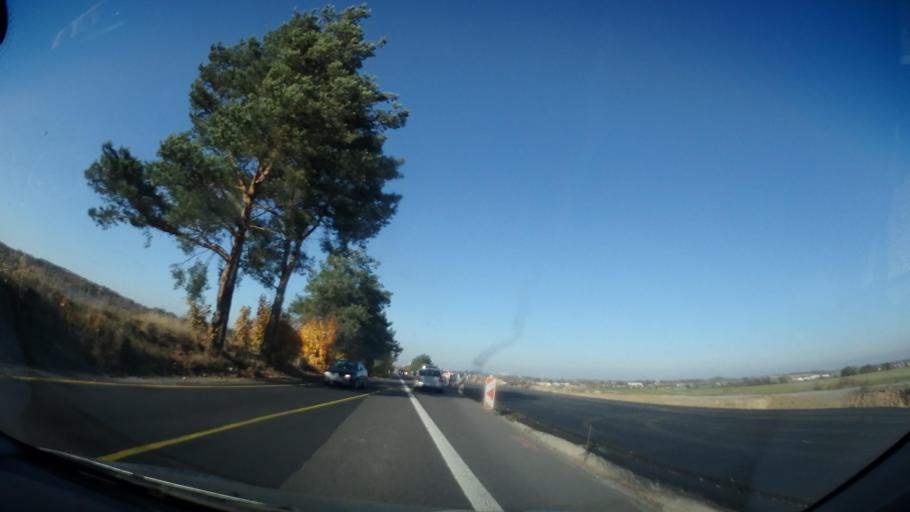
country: CZ
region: Pardubicky
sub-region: Okres Chrudim
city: Slatinany
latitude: 49.9061
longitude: 15.8212
